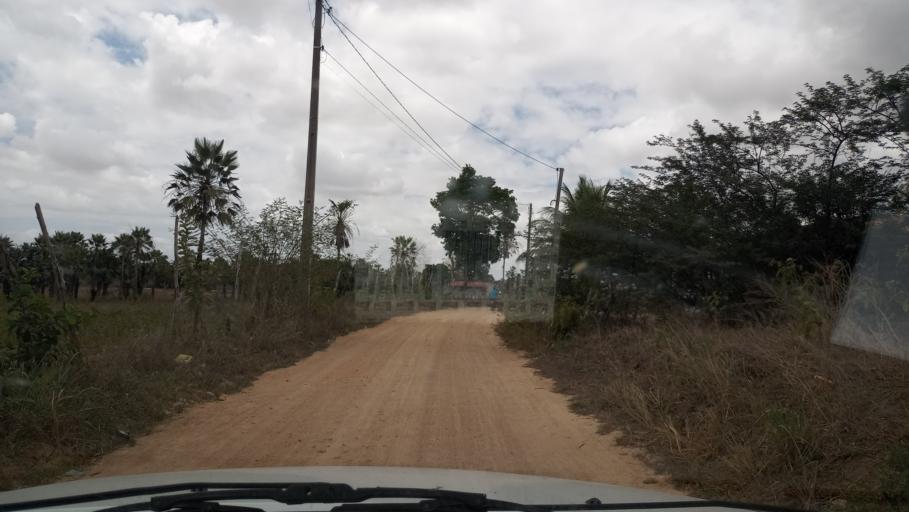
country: BR
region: Rio Grande do Norte
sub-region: Santo Antonio
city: Santo Antonio
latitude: -6.2128
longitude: -35.4644
